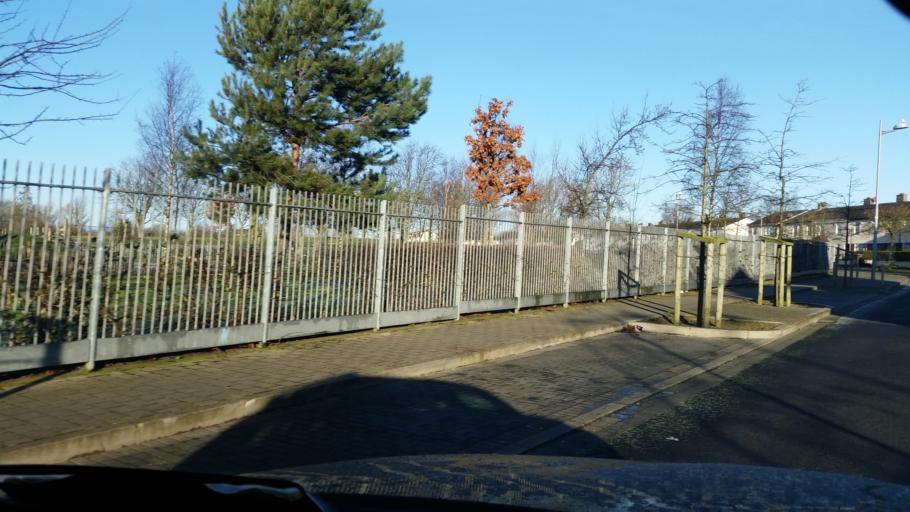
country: IE
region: Leinster
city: Ballymun
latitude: 53.3978
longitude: -6.2788
